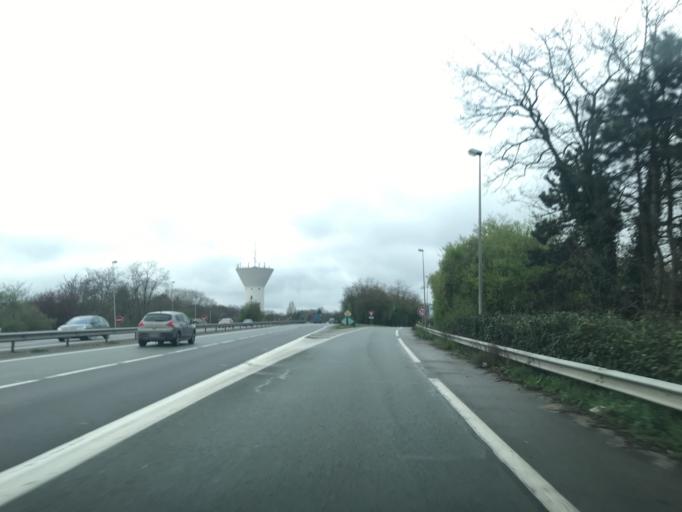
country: FR
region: Centre
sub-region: Departement du Loiret
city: Saint-Jean-de-Braye
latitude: 47.9223
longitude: 1.9951
